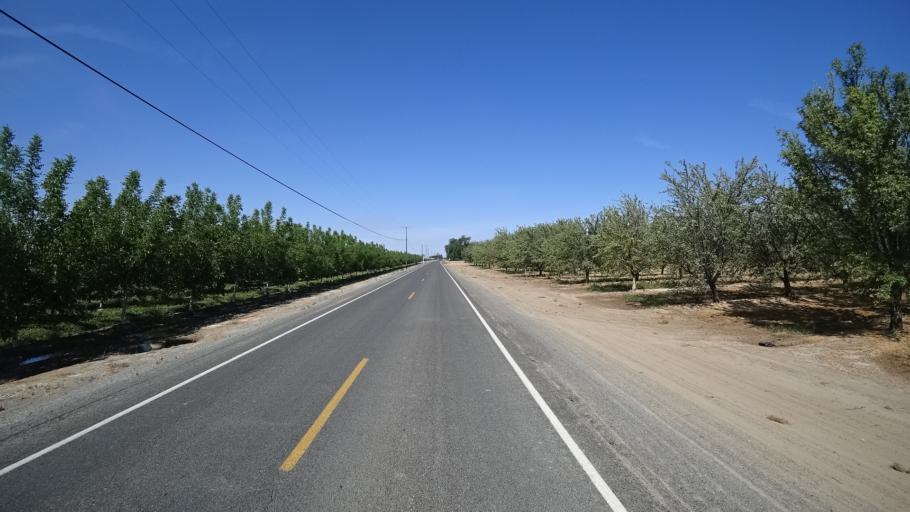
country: US
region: California
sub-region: Kings County
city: Armona
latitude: 36.2547
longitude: -119.7231
